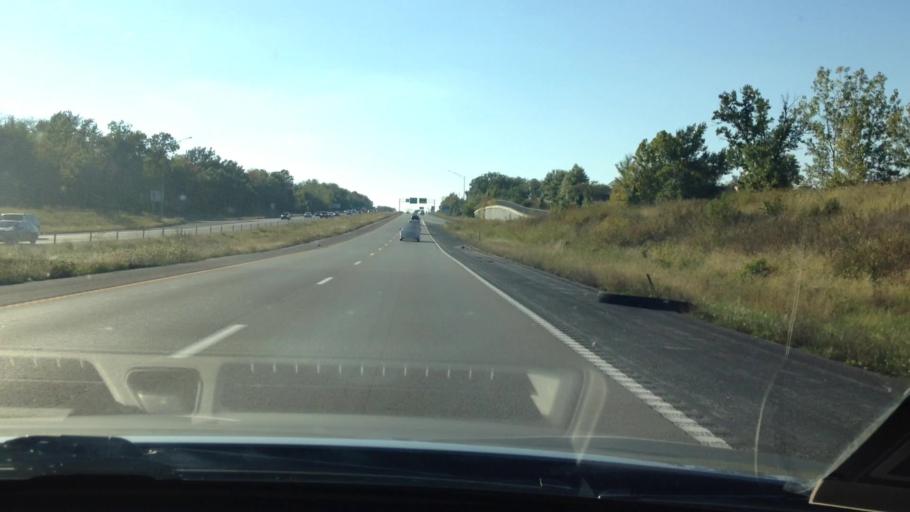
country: US
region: Missouri
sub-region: Platte County
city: Weatherby Lake
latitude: 39.2544
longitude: -94.6336
